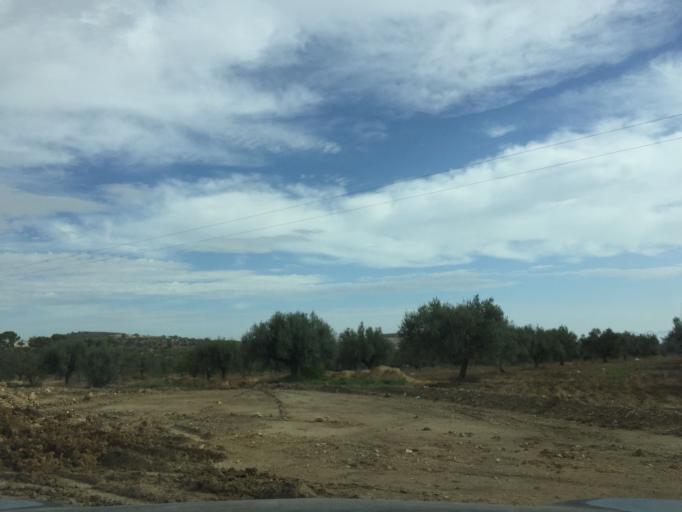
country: TN
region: Zaghwan
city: El Fahs
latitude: 36.2844
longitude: 9.8064
